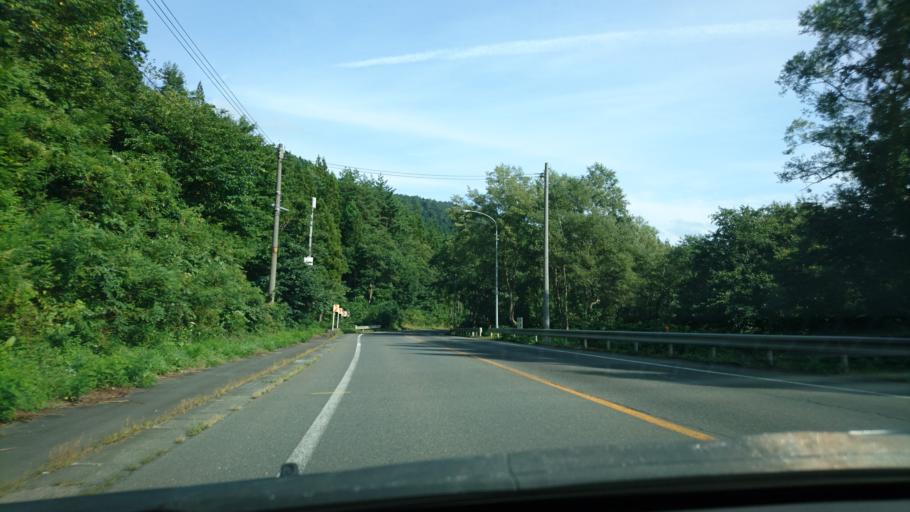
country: JP
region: Akita
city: Yokotemachi
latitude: 39.3130
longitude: 140.8030
